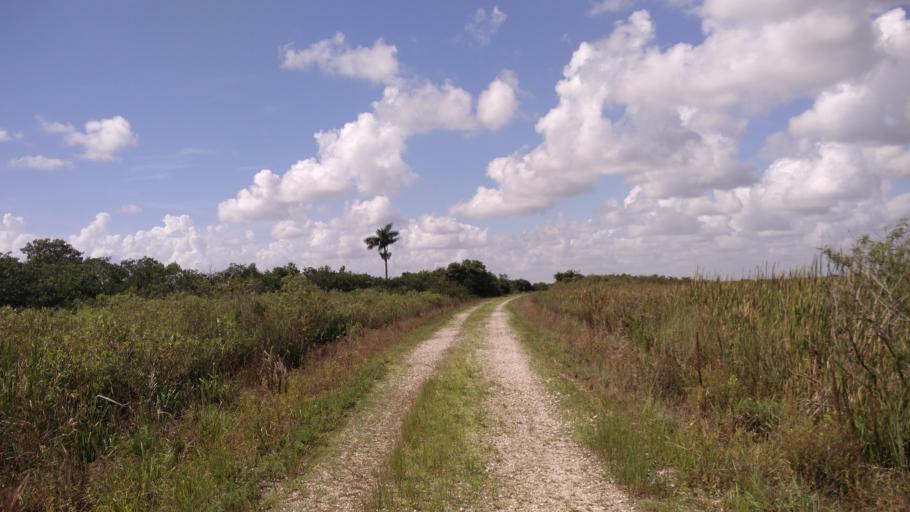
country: US
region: Florida
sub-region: Broward County
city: Weston
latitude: 26.0511
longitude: -80.4615
